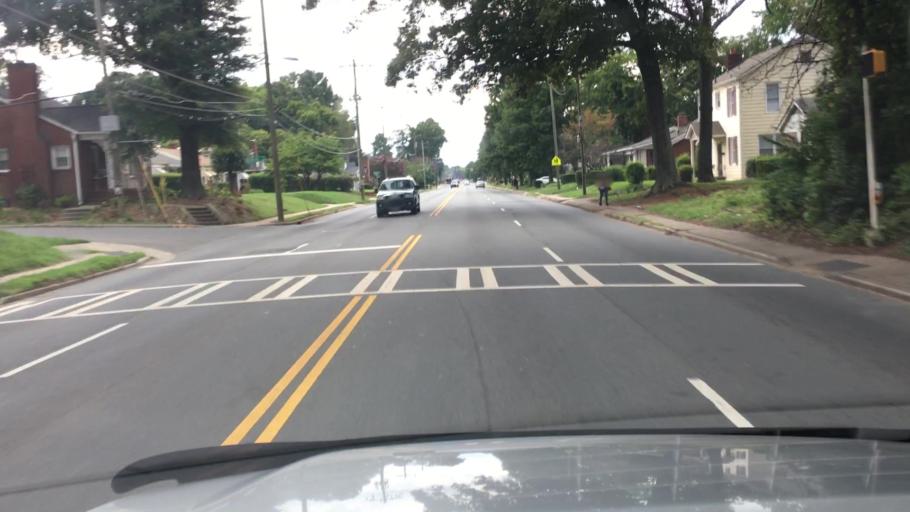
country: US
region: North Carolina
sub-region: Mecklenburg County
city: Charlotte
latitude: 35.2602
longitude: -80.8552
